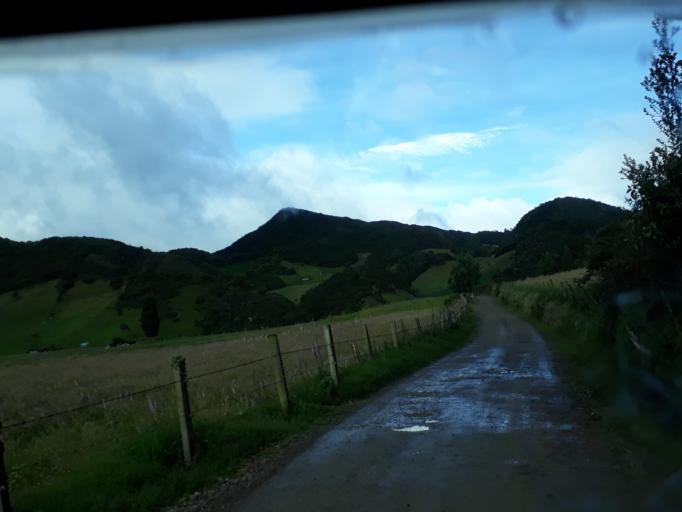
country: CO
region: Cundinamarca
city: Sutatausa
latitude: 5.1850
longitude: -73.9022
